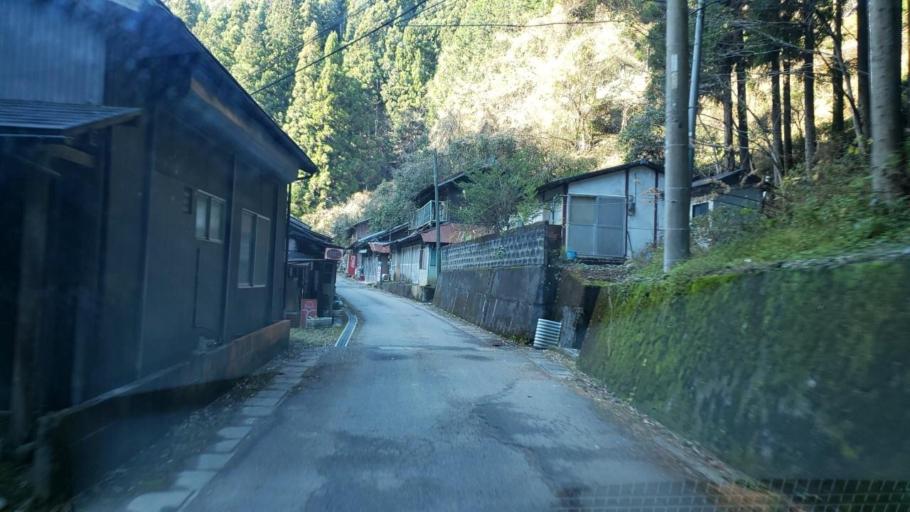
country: JP
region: Tokushima
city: Wakimachi
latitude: 33.9895
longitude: 133.9919
